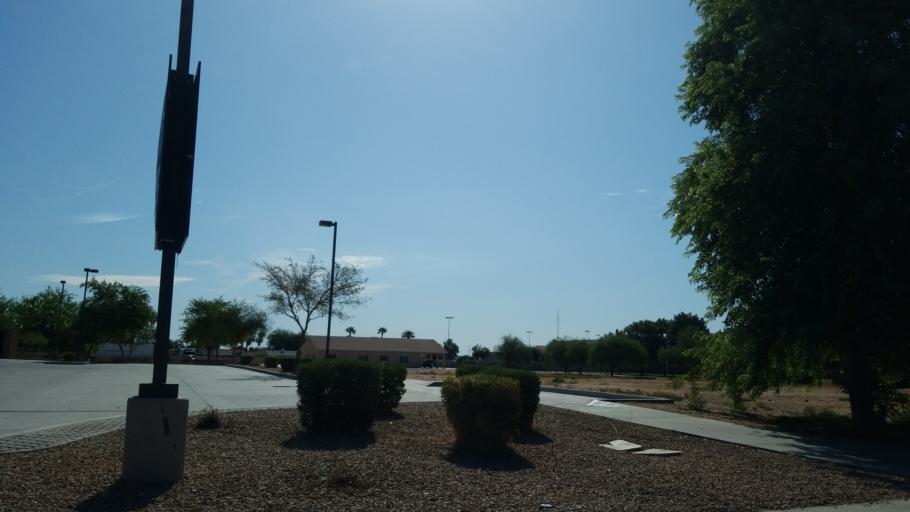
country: US
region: Arizona
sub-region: Maricopa County
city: Glendale
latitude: 33.4919
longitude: -112.2196
